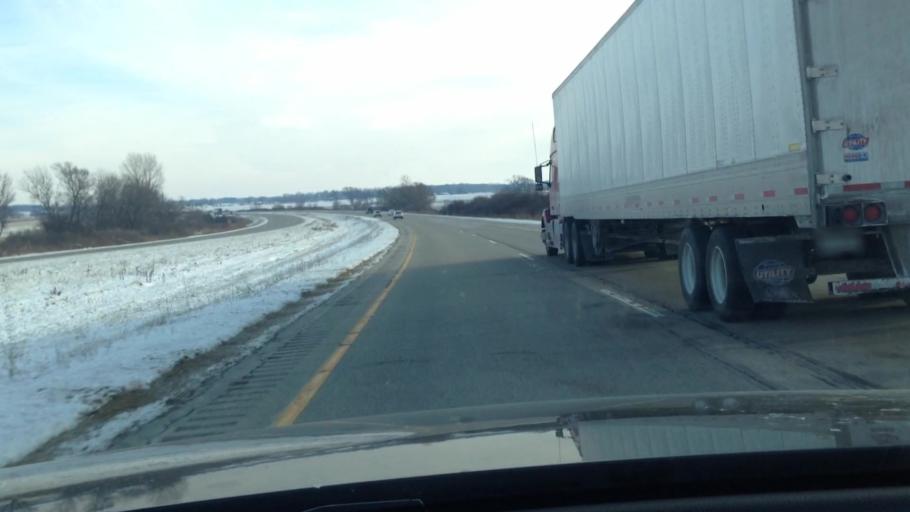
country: US
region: Wisconsin
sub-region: Walworth County
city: Como
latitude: 42.6492
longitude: -88.5051
